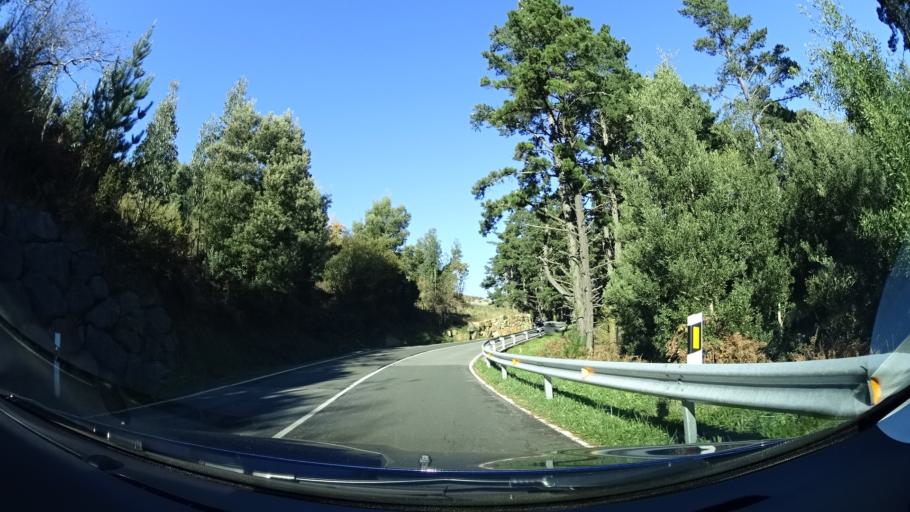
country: ES
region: Basque Country
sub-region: Bizkaia
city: Bermeo
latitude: 43.4416
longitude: -2.7540
